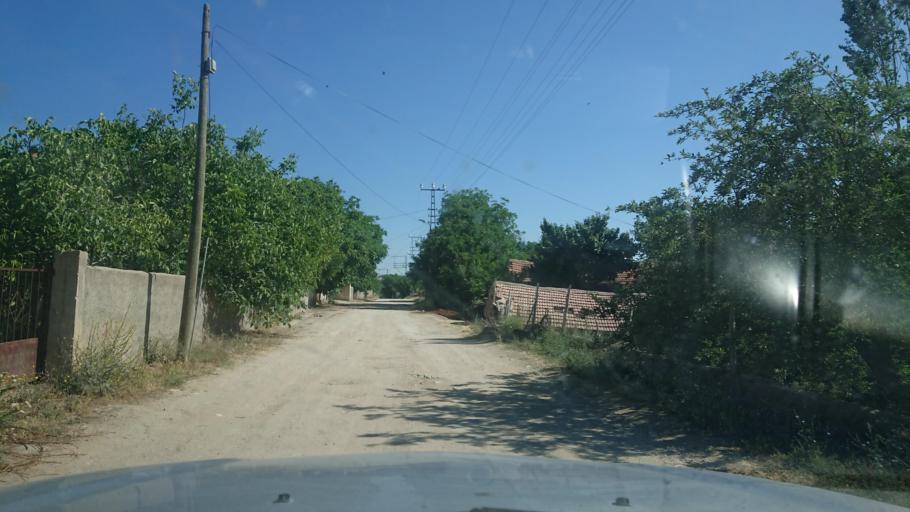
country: TR
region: Aksaray
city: Agacoren
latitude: 38.8666
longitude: 33.9139
